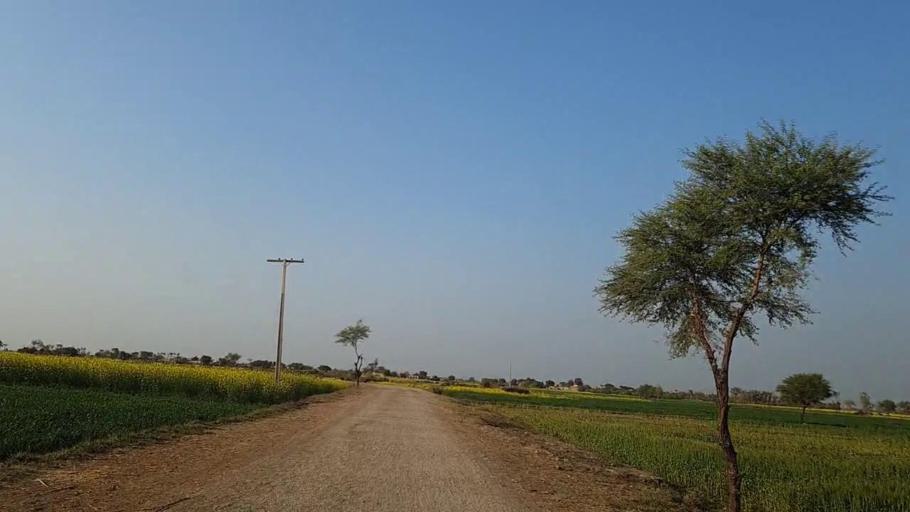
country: PK
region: Sindh
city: Sakrand
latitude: 26.1074
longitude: 68.3694
